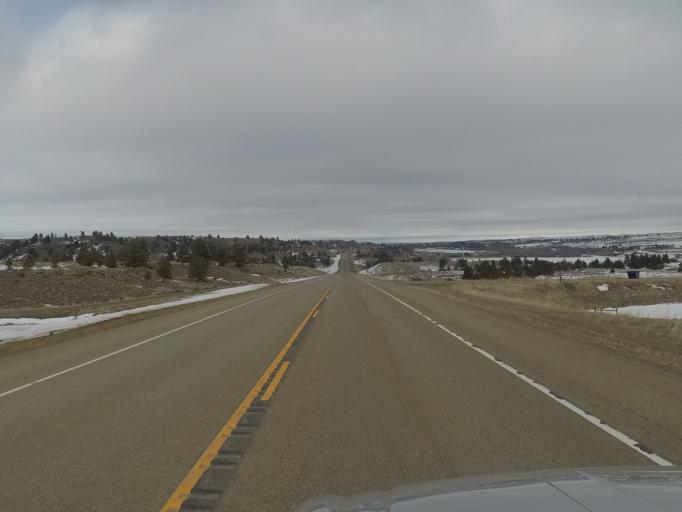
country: US
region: Montana
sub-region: Golden Valley County
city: Ryegate
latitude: 46.3177
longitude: -109.1520
